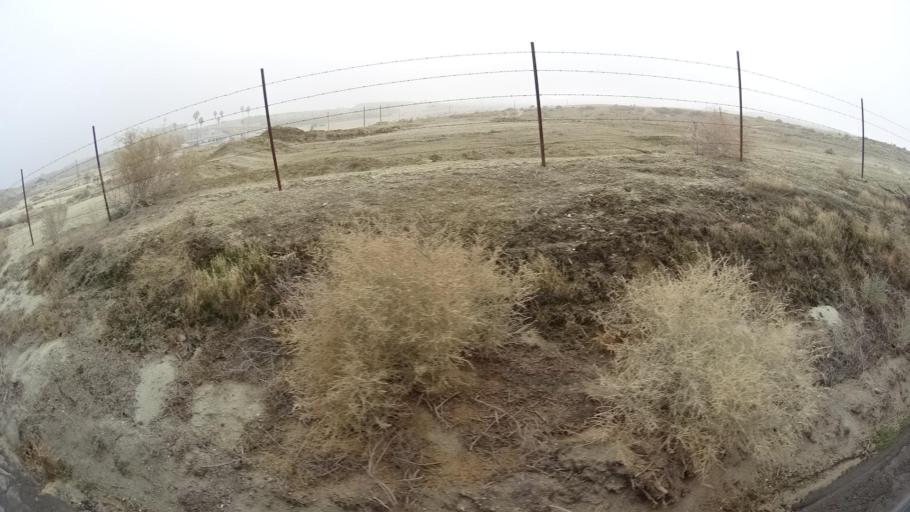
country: US
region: California
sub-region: Kern County
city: Ford City
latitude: 35.1648
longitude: -119.3836
